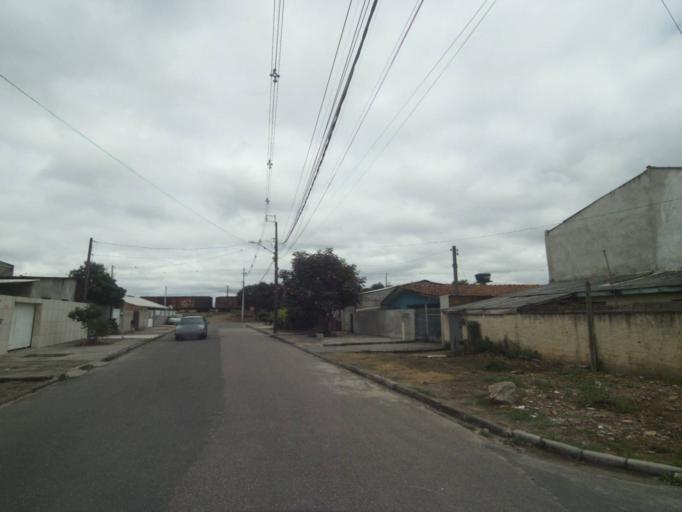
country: BR
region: Parana
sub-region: Pinhais
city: Pinhais
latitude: -25.4567
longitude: -49.1991
